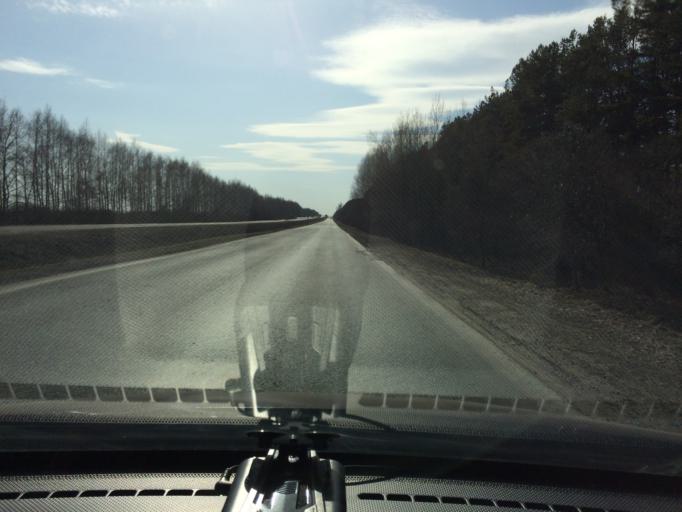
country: RU
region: Mariy-El
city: Yoshkar-Ola
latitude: 56.7329
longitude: 48.1547
